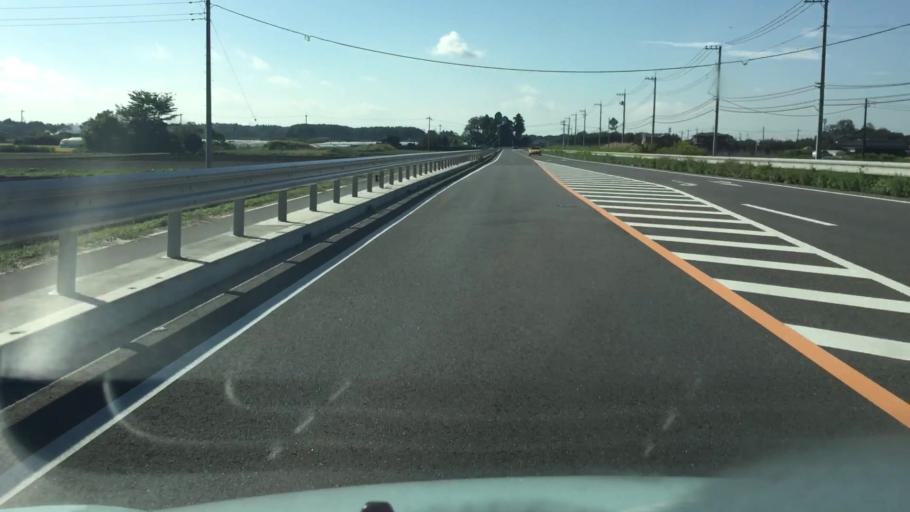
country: JP
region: Tochigi
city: Ujiie
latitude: 36.5973
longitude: 139.9848
